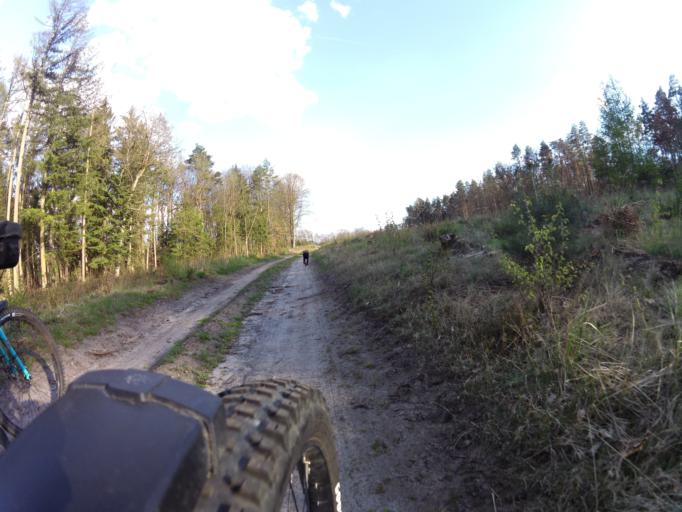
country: PL
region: West Pomeranian Voivodeship
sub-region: Powiat gryficki
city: Ploty
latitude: 53.7607
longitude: 15.2668
